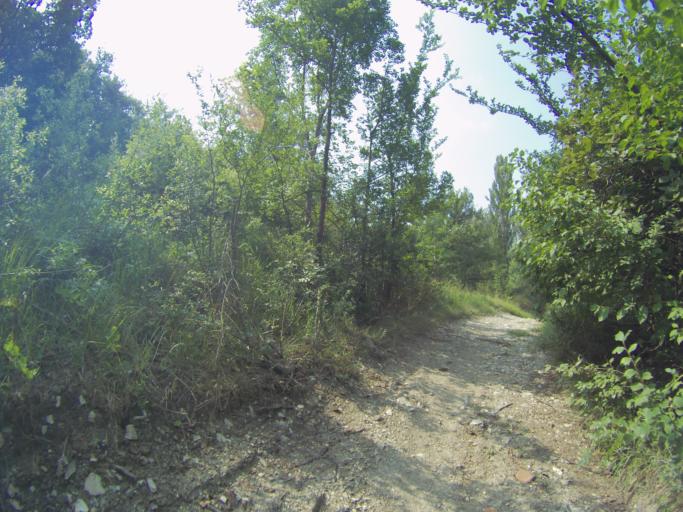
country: IT
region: Emilia-Romagna
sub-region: Provincia di Reggio Emilia
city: Ventoso
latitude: 44.5690
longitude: 10.6540
